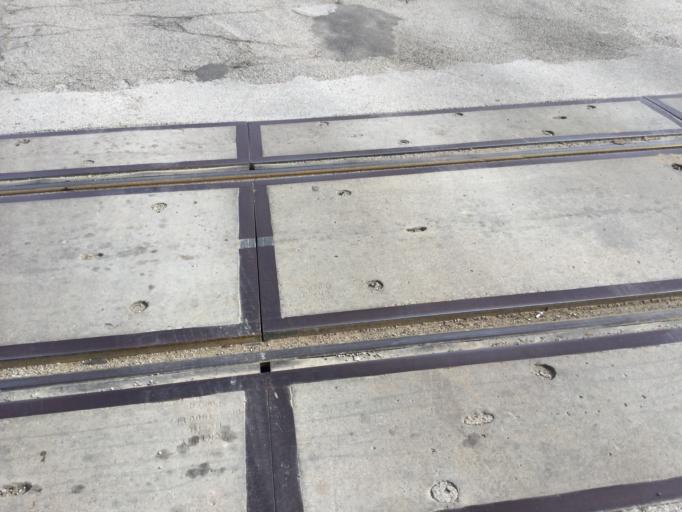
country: US
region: Kansas
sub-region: Cherokee County
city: Columbus
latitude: 37.1756
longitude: -94.8499
